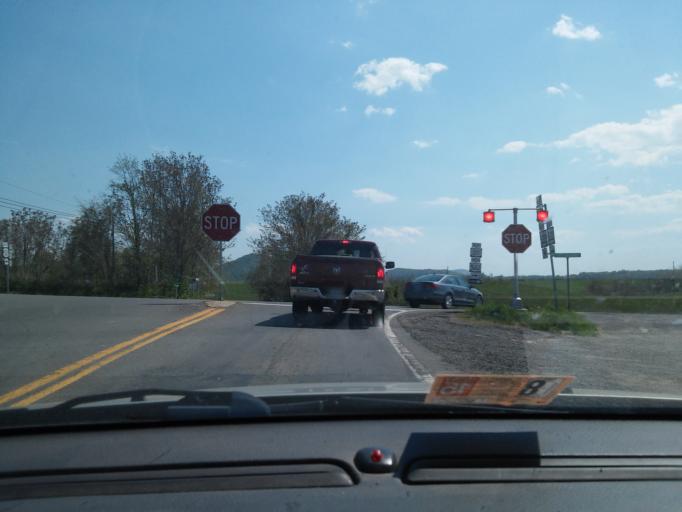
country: US
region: Virginia
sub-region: Rappahannock County
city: Washington
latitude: 38.7240
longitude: -78.1143
